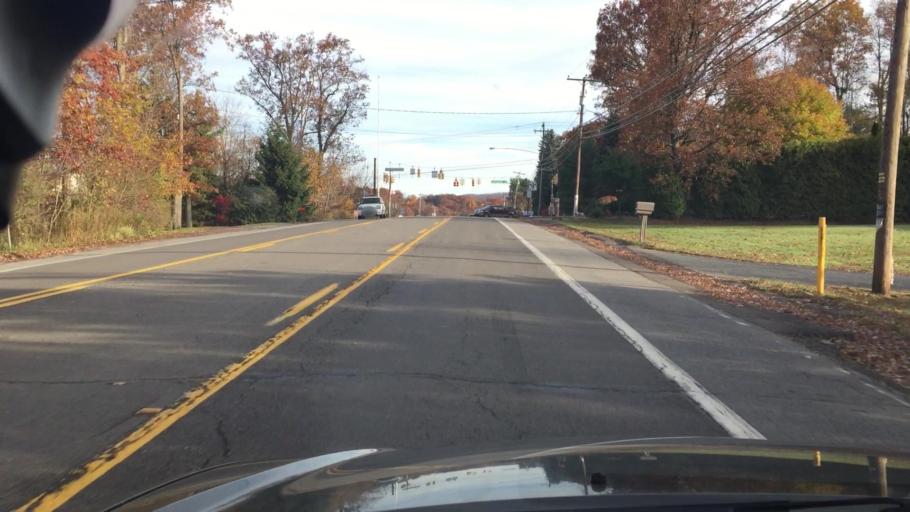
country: US
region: Pennsylvania
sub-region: Luzerne County
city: Mountain Top
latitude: 41.1421
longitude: -75.9006
